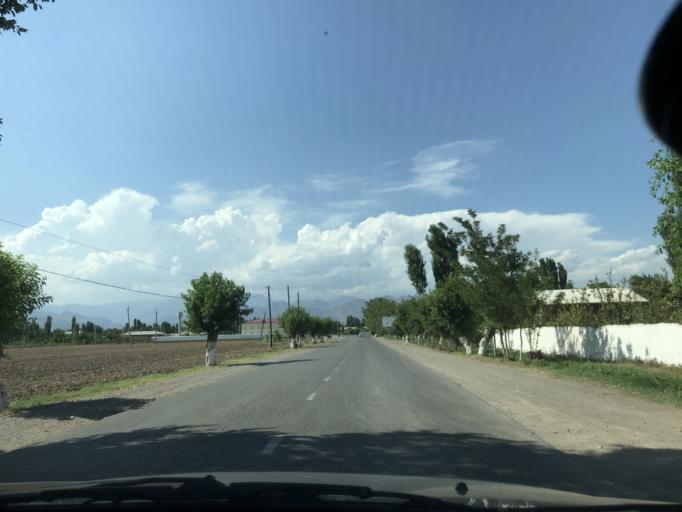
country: UZ
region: Namangan
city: Chust Shahri
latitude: 41.0633
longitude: 71.2069
